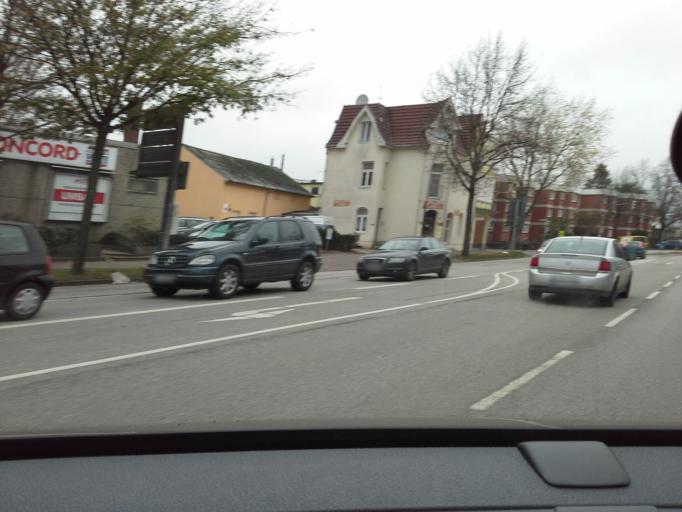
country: DE
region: Schleswig-Holstein
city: Pinneberg
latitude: 53.6643
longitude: 9.7932
